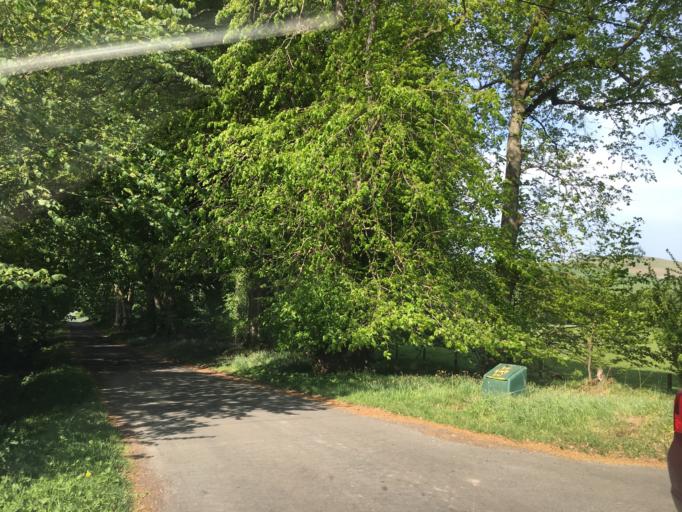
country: GB
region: Scotland
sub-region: South Lanarkshire
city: Biggar
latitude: 55.6208
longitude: -3.4048
